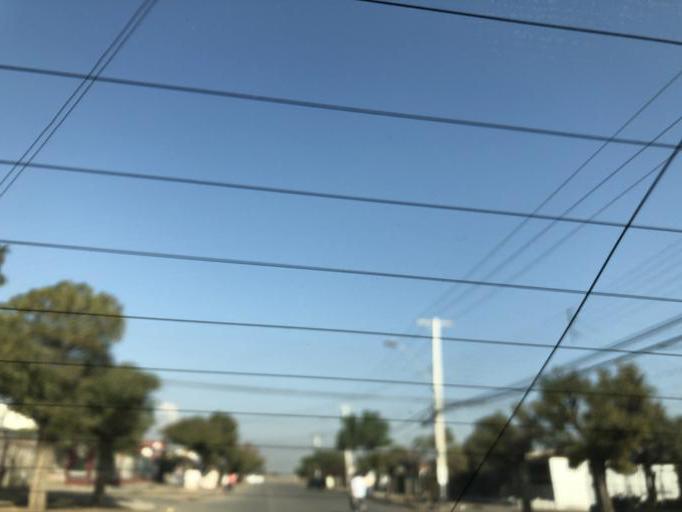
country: CL
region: Santiago Metropolitan
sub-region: Provincia de Cordillera
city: Puente Alto
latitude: -33.6166
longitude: -70.5630
